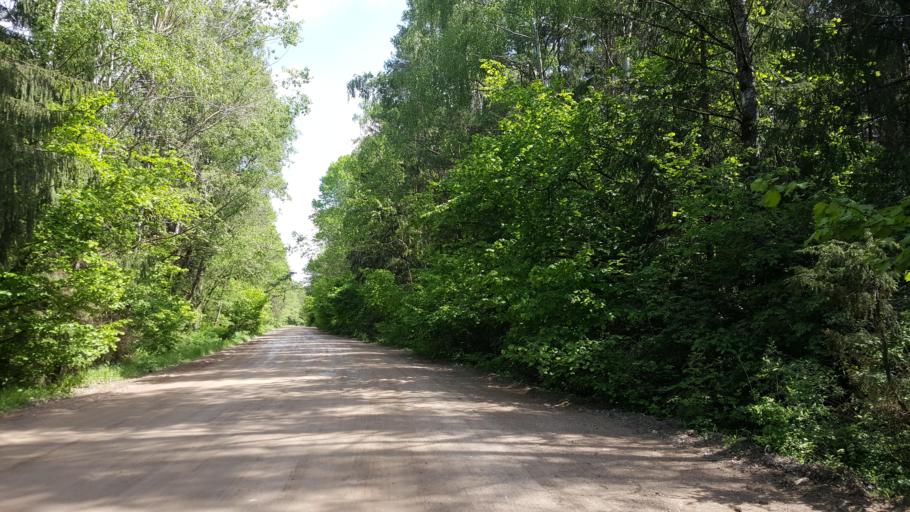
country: BY
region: Brest
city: Kamyanyets
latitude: 52.4223
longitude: 23.9554
